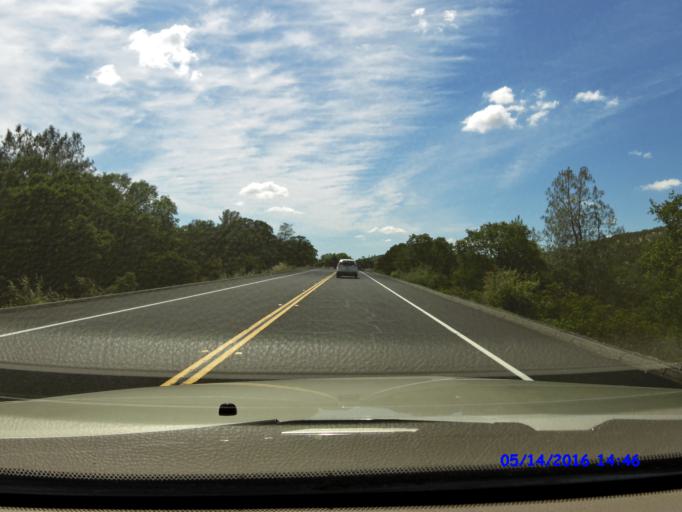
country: US
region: California
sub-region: Tuolumne County
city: Jamestown
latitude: 37.8504
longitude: -120.3967
